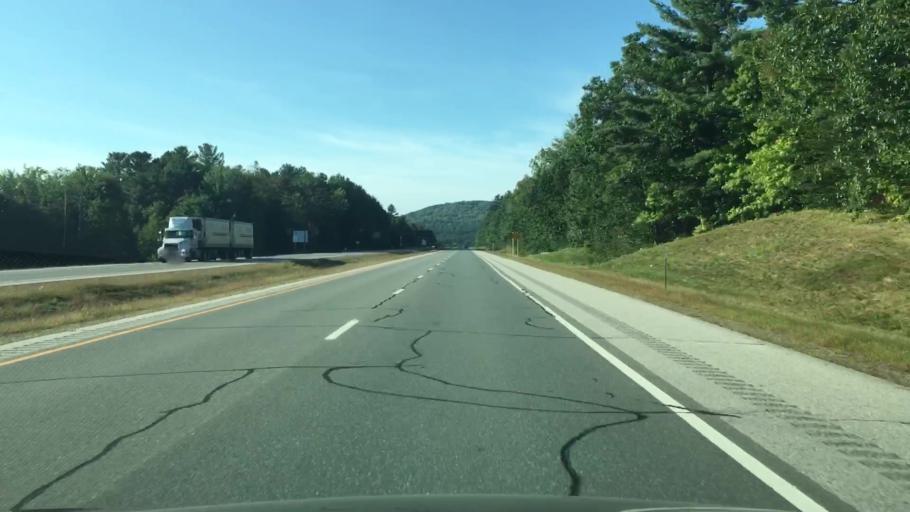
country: US
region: New Hampshire
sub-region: Grafton County
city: Littleton
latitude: 44.2350
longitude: -71.7542
